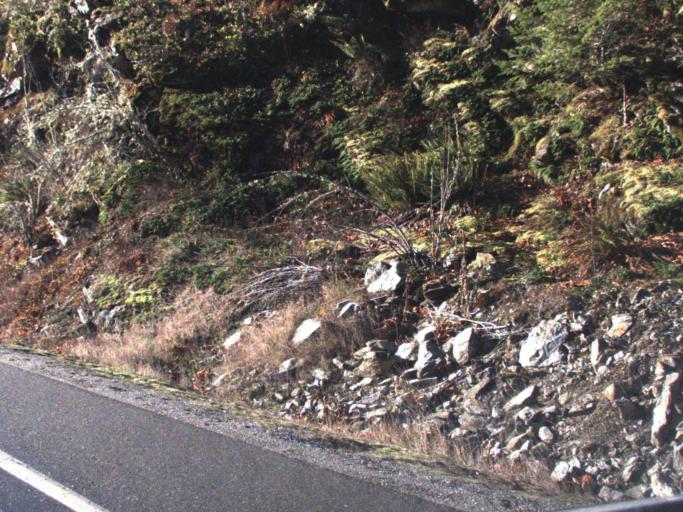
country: US
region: Washington
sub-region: Snohomish County
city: Darrington
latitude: 48.5790
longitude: -121.4065
